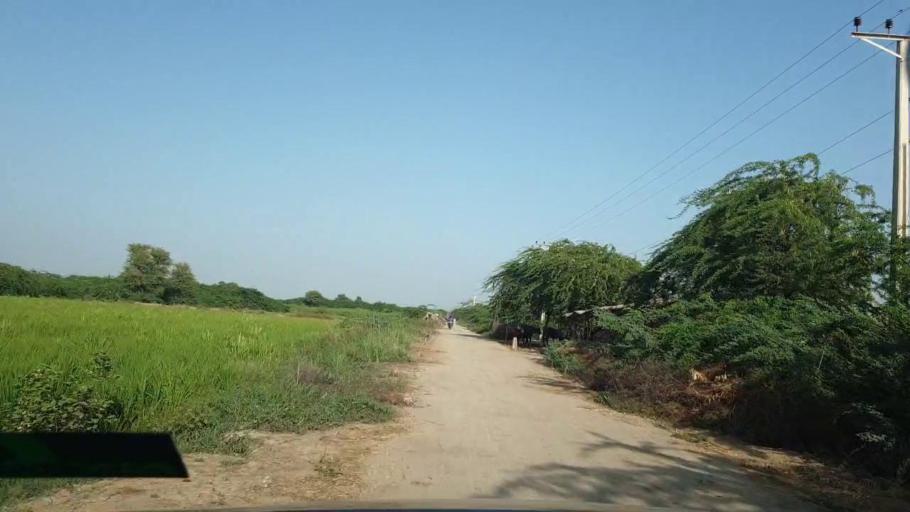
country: PK
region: Sindh
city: Naukot
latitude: 24.7407
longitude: 69.2361
